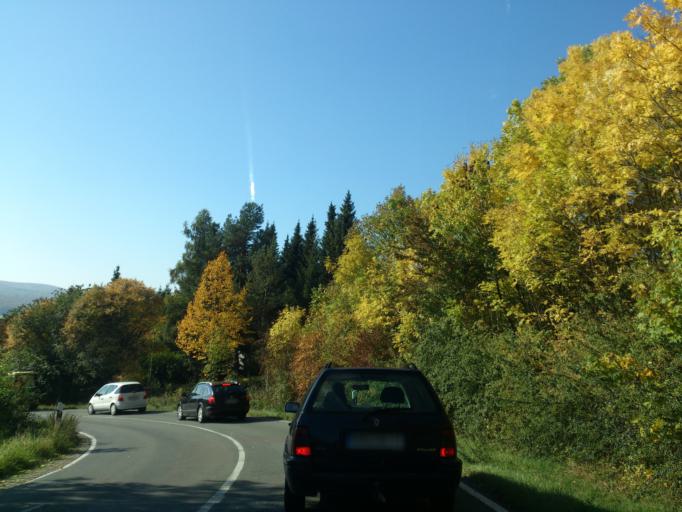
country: DE
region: Hesse
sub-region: Regierungsbezirk Kassel
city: Calden
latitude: 51.3746
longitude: 9.4165
